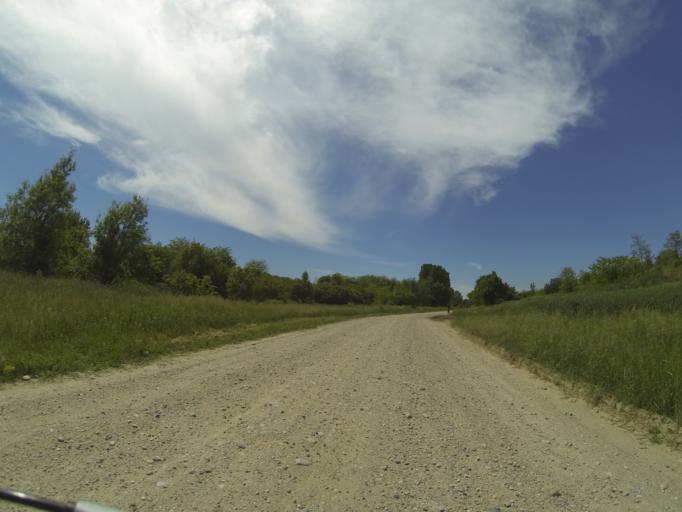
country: RO
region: Dolj
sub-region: Comuna Teslui
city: Teslui
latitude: 44.1986
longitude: 24.1254
